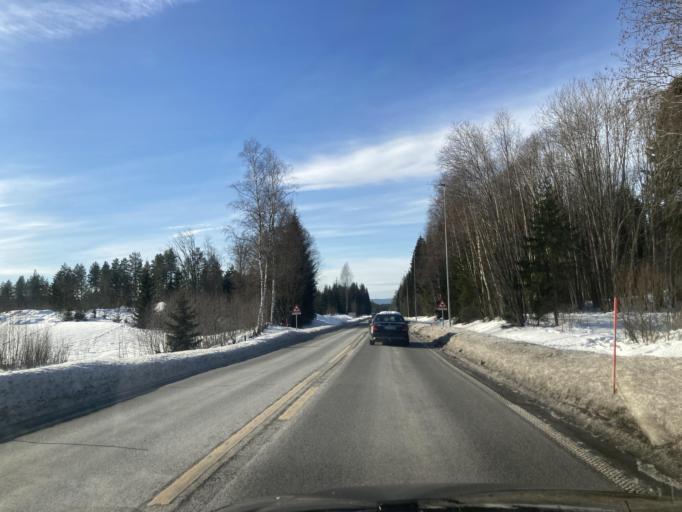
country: NO
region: Hedmark
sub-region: Elverum
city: Elverum
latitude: 60.9191
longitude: 11.6547
